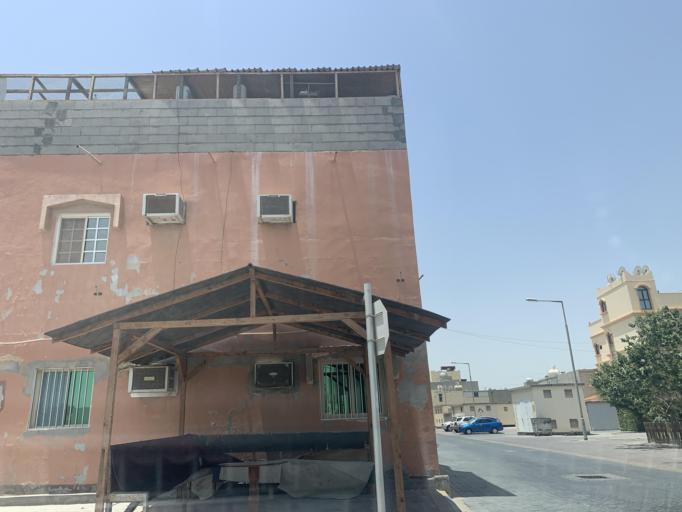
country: BH
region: Northern
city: Sitrah
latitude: 26.1592
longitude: 50.6234
